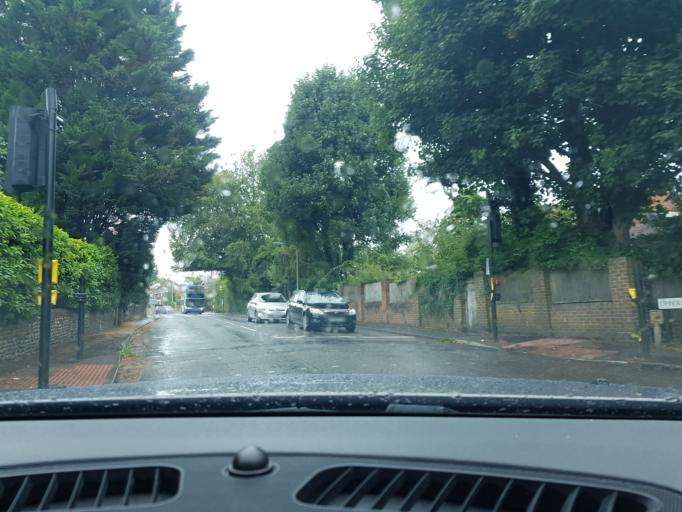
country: GB
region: England
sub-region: Surrey
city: Hale
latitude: 51.2284
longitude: -0.7848
